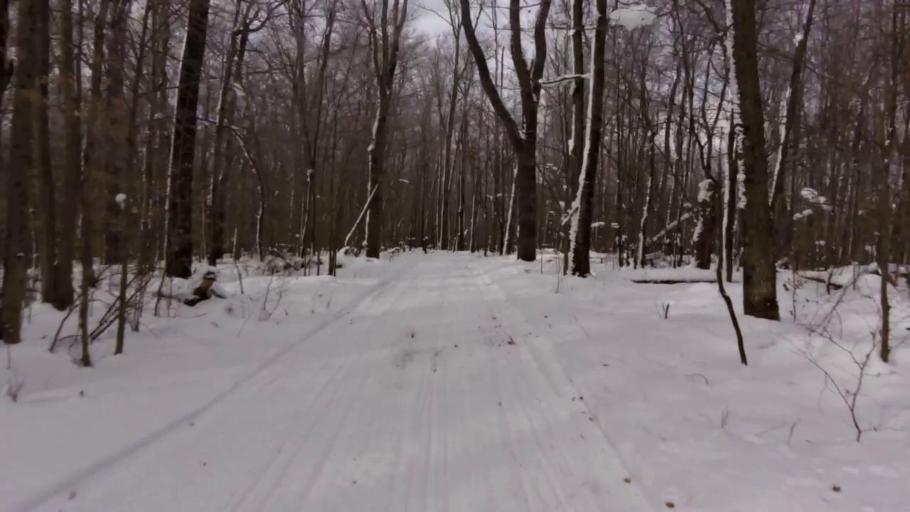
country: US
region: New York
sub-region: Cattaraugus County
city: Salamanca
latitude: 42.0339
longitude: -78.7505
